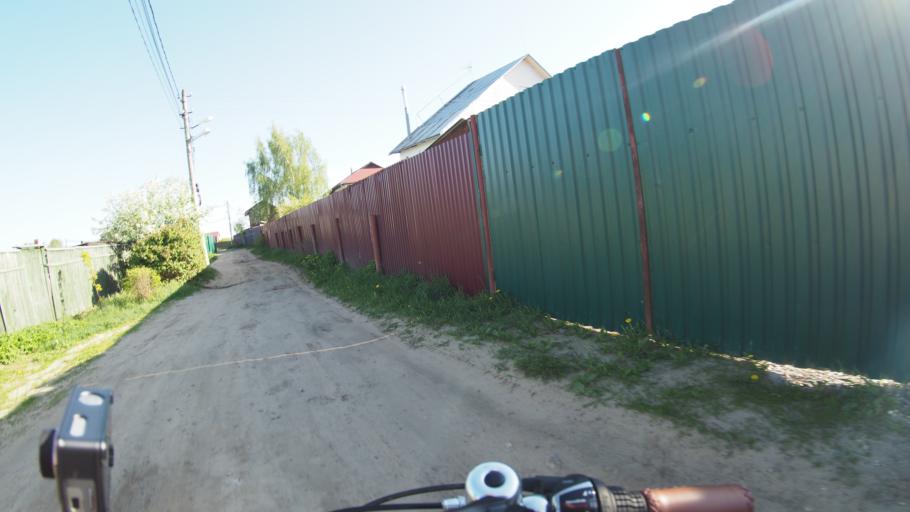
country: RU
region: Moskovskaya
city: Ramenskoye
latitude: 55.5457
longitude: 38.1947
